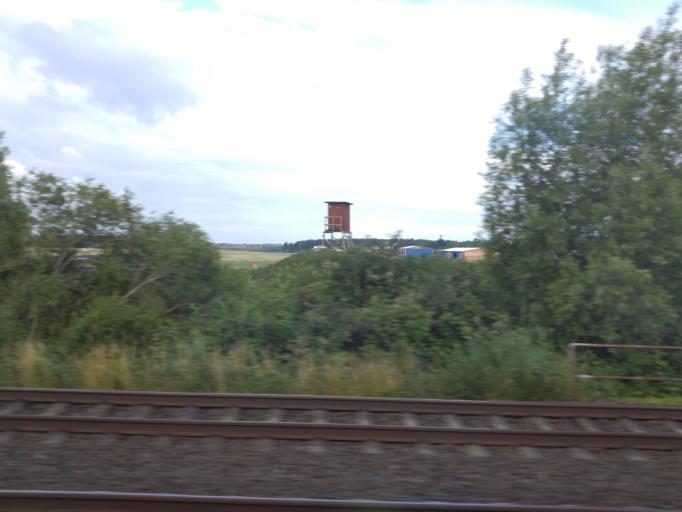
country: DE
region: Hesse
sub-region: Regierungsbezirk Darmstadt
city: Erzhausen
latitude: 49.9618
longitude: 8.6524
